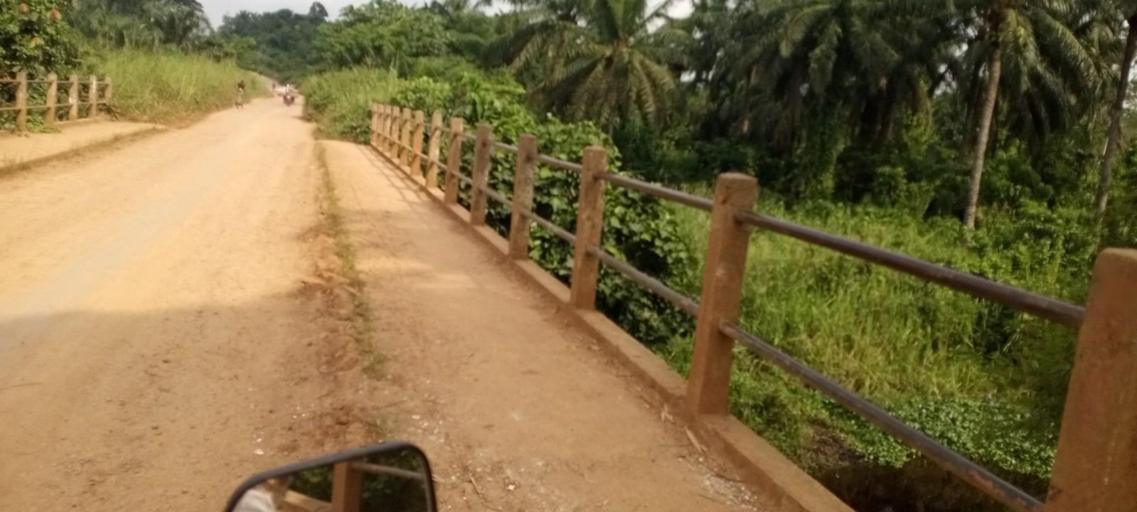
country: CD
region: Eastern Province
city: Kisangani
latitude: 0.3898
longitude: 25.3879
